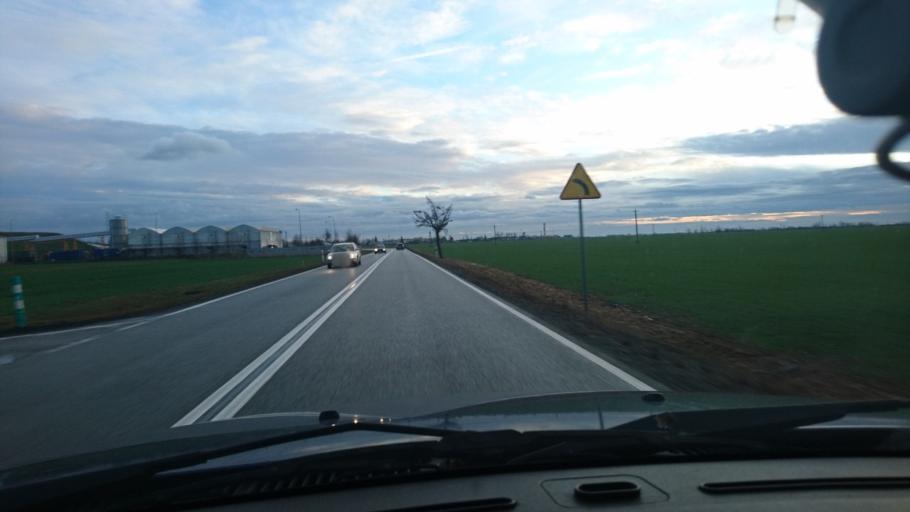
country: PL
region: Opole Voivodeship
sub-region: Powiat kluczborski
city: Kluczbork
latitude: 51.0041
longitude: 18.2049
